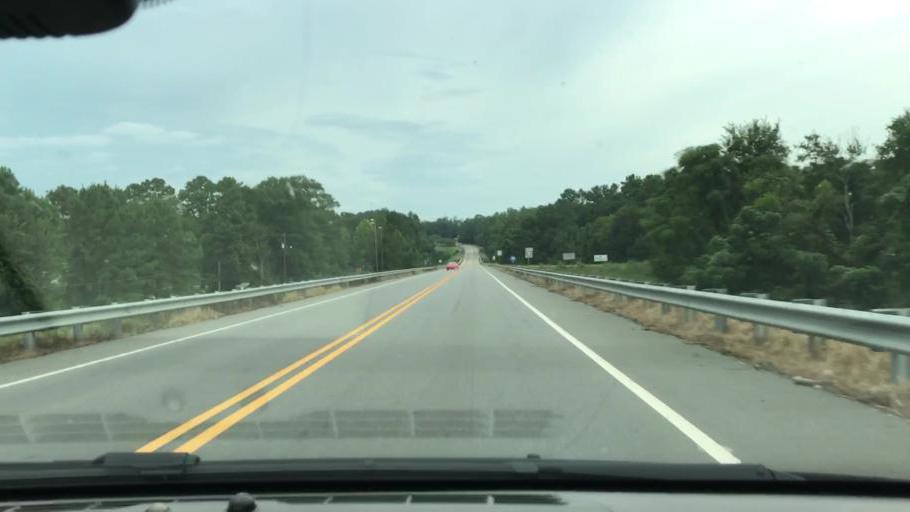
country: US
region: Alabama
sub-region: Houston County
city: Ashford
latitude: 31.2863
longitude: -85.1014
